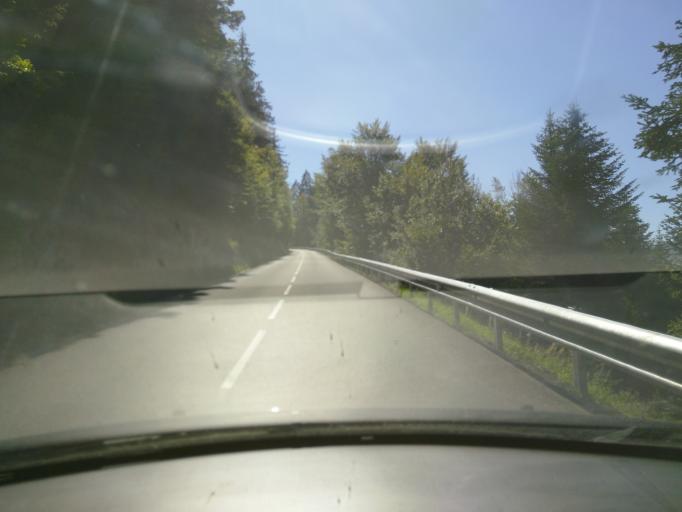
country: FR
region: Rhone-Alpes
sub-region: Departement de la Savoie
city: Ugine
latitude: 45.7916
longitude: 6.4951
